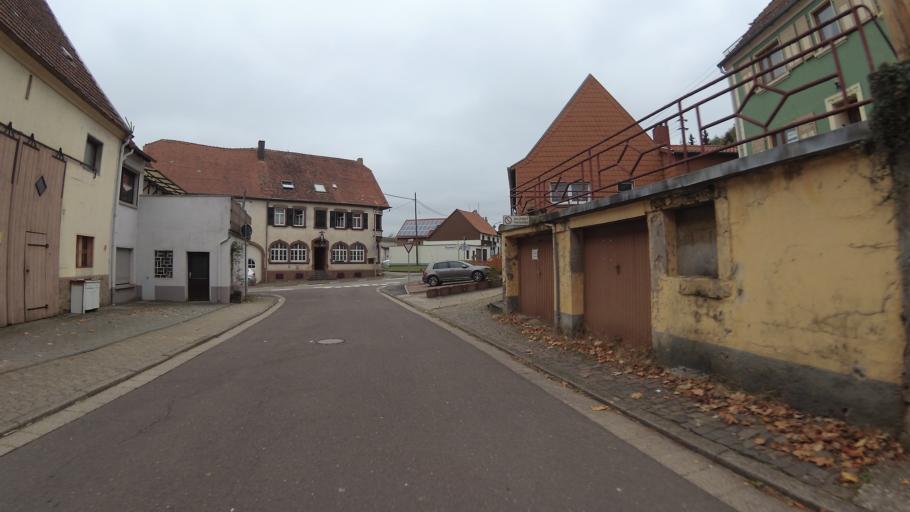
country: DE
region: Saarland
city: Blieskastel
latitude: 49.2415
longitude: 7.2732
